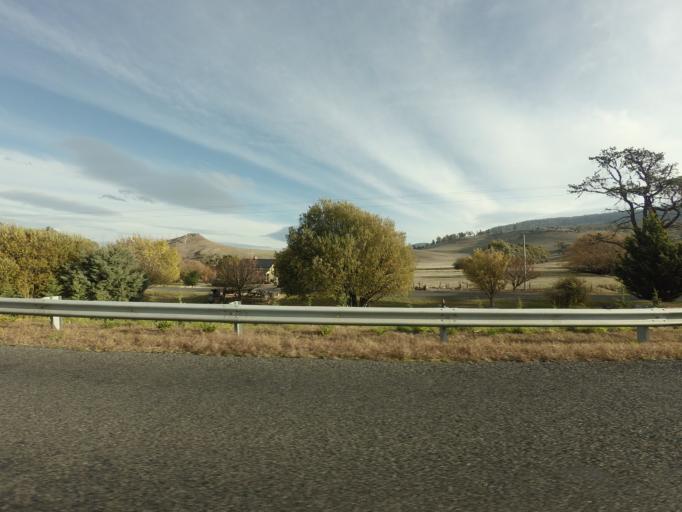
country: AU
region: Tasmania
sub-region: Brighton
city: Bridgewater
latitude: -42.4380
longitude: 147.1500
